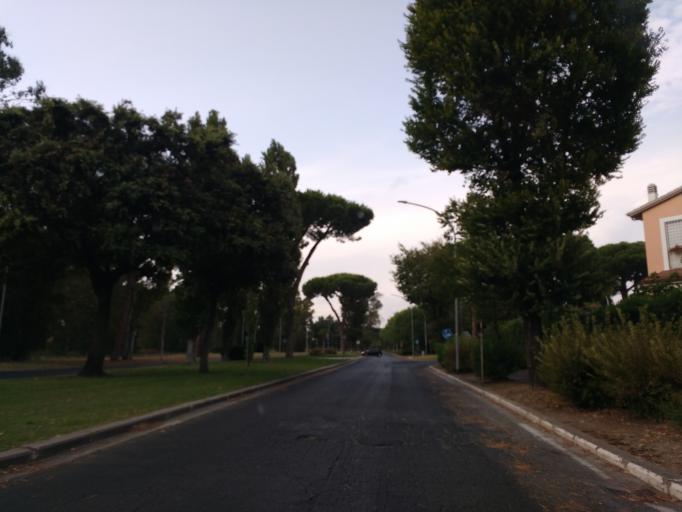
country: IT
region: Latium
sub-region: Citta metropolitana di Roma Capitale
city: Acilia-Castel Fusano-Ostia Antica
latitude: 41.7544
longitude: 12.3507
